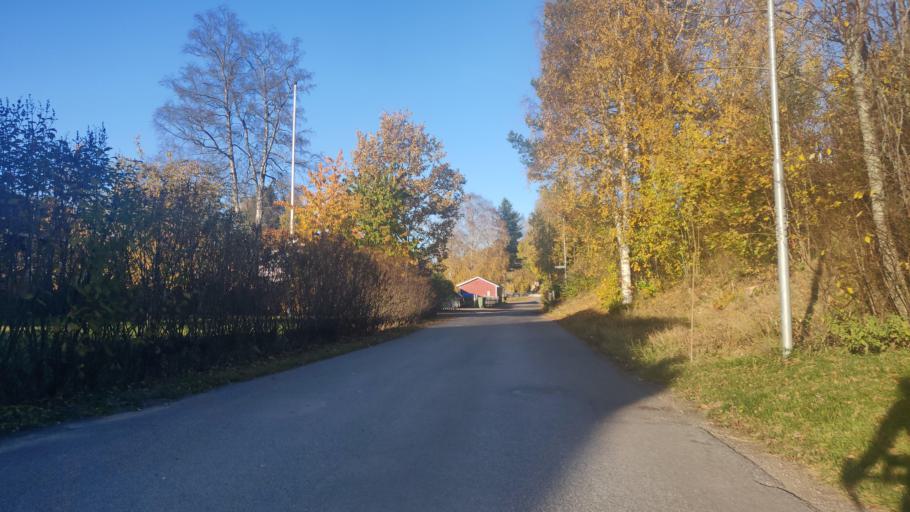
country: SE
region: Vaesternorrland
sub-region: Sundsvalls Kommun
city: Skottsund
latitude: 62.2898
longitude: 17.3856
